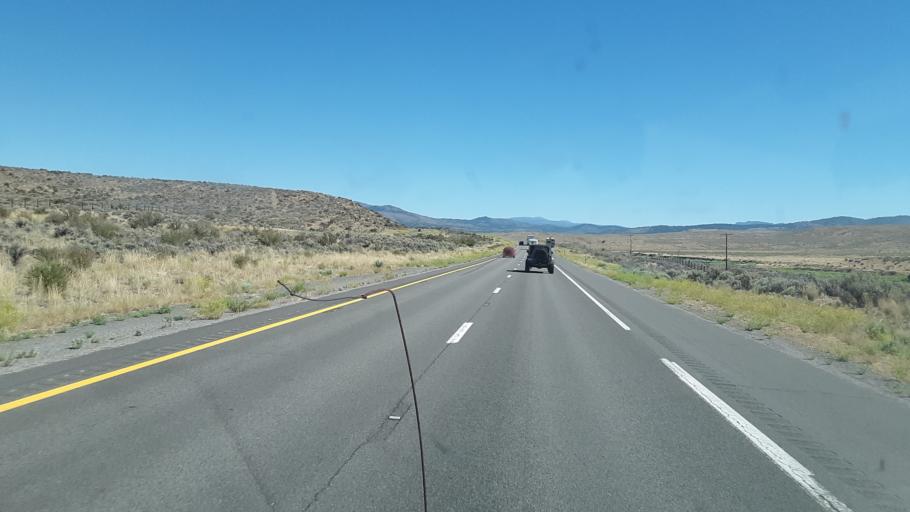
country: US
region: Nevada
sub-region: Washoe County
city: Cold Springs
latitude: 39.7072
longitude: -120.0349
